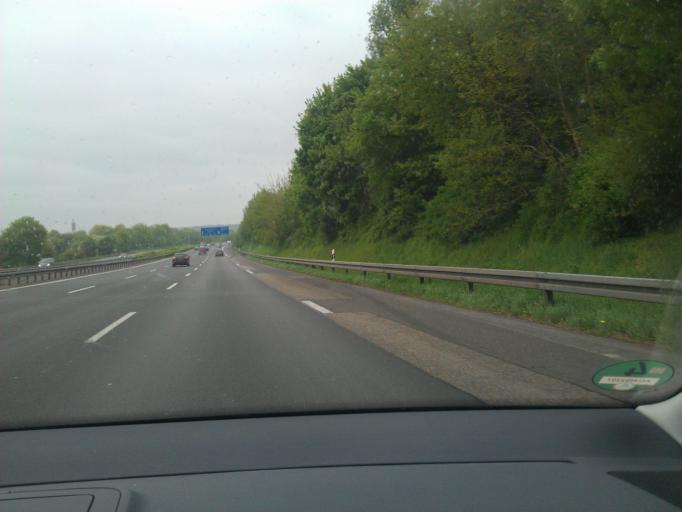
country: DE
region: North Rhine-Westphalia
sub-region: Regierungsbezirk Koln
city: Stossdorf
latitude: 50.7883
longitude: 7.2375
